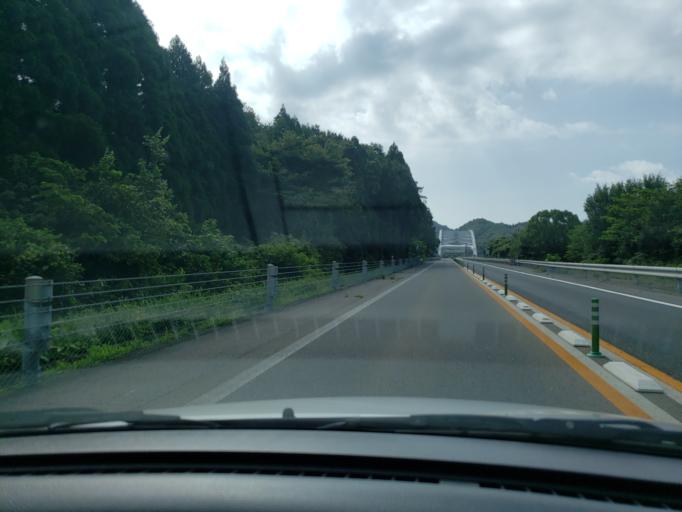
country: JP
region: Hiroshima
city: Innoshima
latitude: 34.2185
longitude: 133.0521
